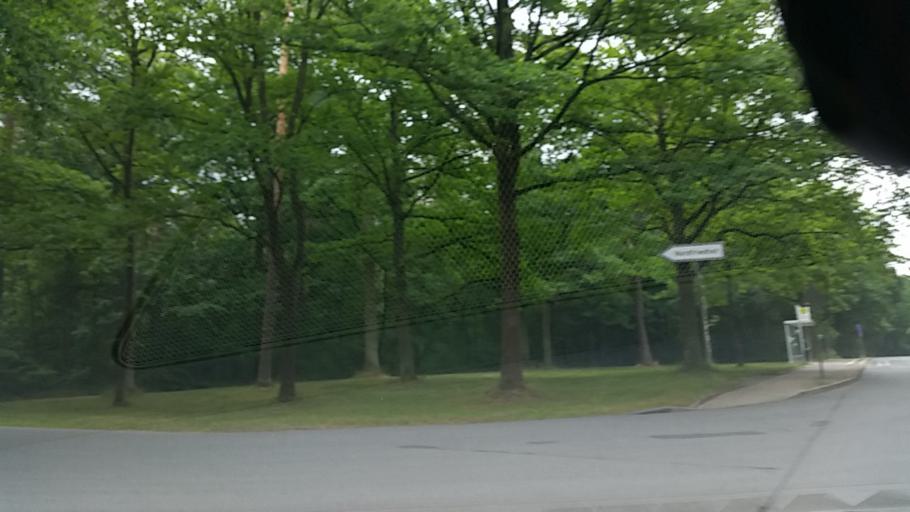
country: DE
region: Lower Saxony
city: Wolfsburg
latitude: 52.4606
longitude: 10.8013
